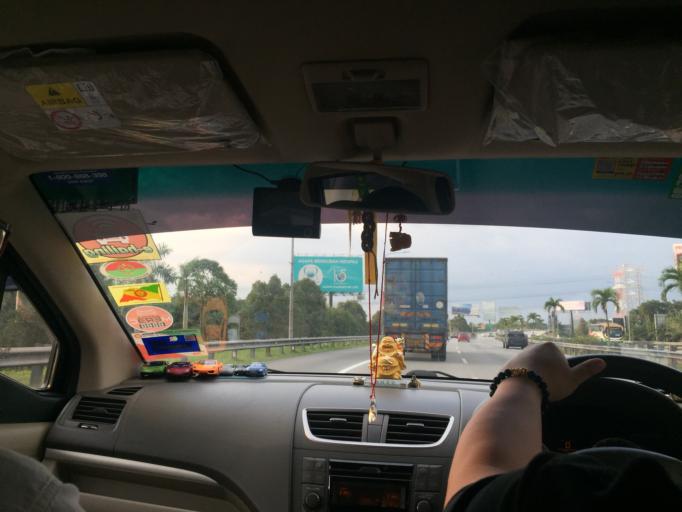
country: MY
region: Putrajaya
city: Putrajaya
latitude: 2.8185
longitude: 101.6627
